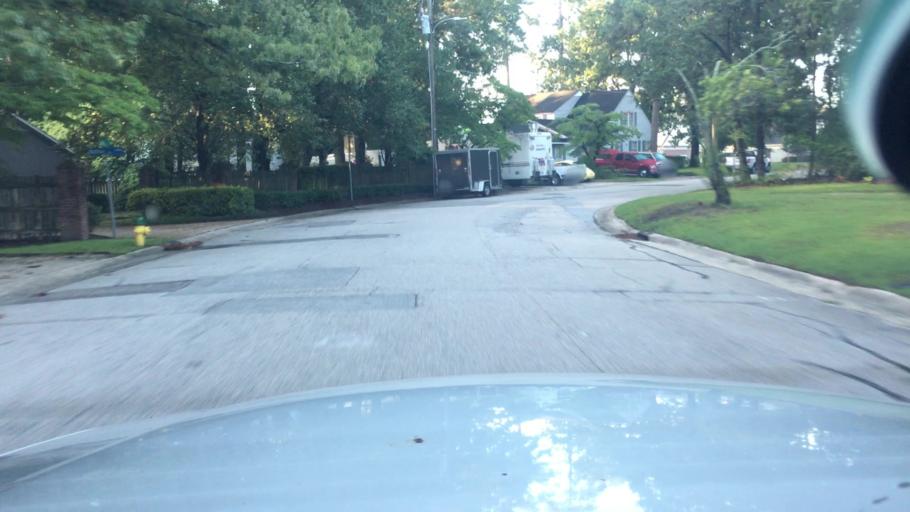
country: US
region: North Carolina
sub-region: Cumberland County
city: Fayetteville
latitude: 35.0682
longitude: -78.9171
